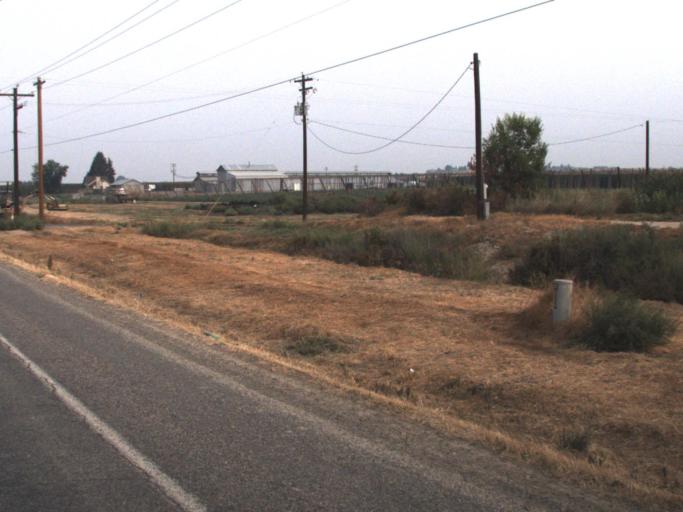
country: US
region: Washington
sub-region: Yakima County
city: Mabton
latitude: 46.2393
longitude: -119.9995
